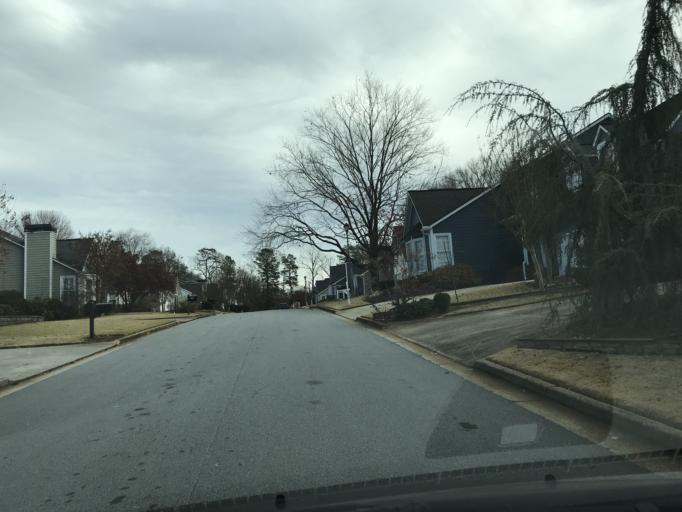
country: US
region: Georgia
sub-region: DeKalb County
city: North Atlanta
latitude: 33.8774
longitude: -84.3446
